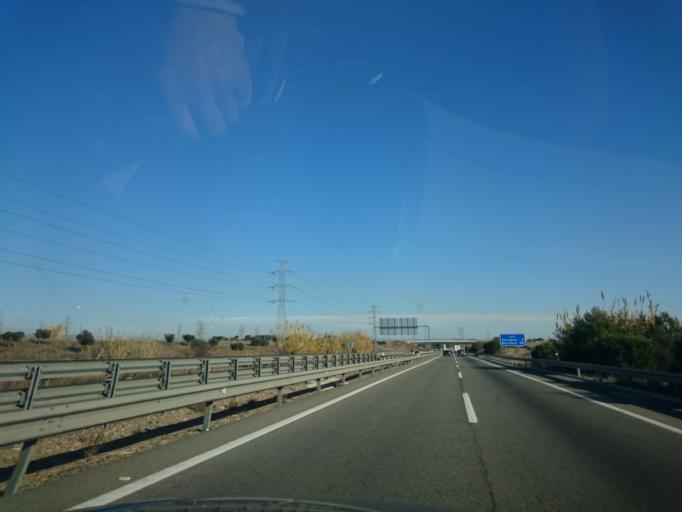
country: ES
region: Catalonia
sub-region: Provincia de Tarragona
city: Vila-seca
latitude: 41.1244
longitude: 1.1652
